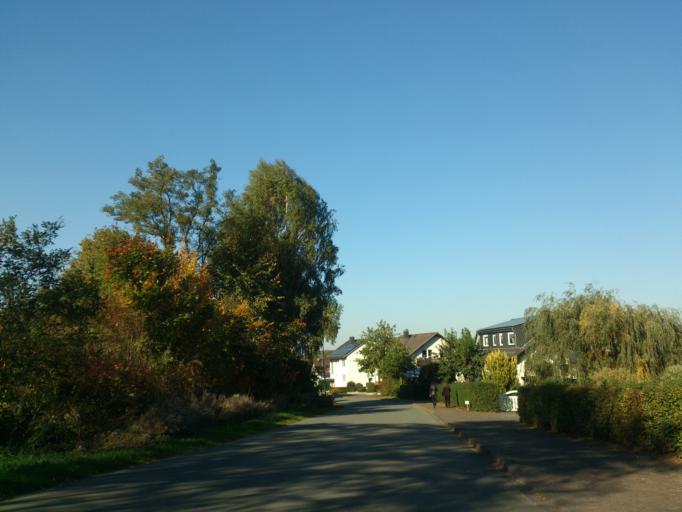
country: DE
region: North Rhine-Westphalia
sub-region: Regierungsbezirk Detmold
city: Willebadessen
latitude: 51.5765
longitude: 9.0377
